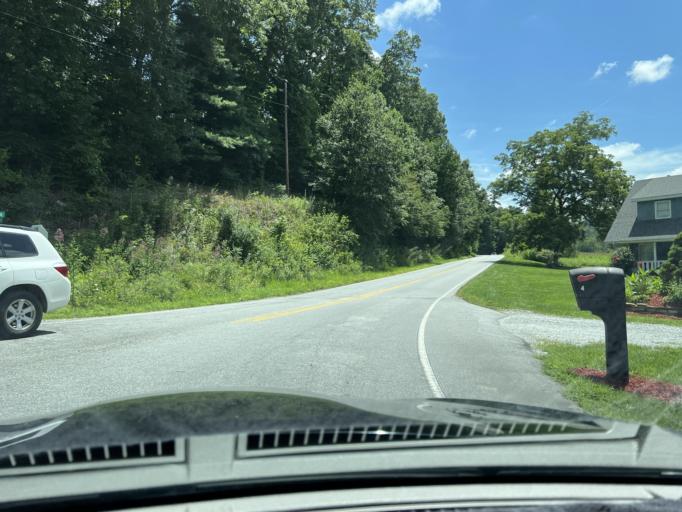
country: US
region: North Carolina
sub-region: Henderson County
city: Hoopers Creek
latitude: 35.4402
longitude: -82.4398
